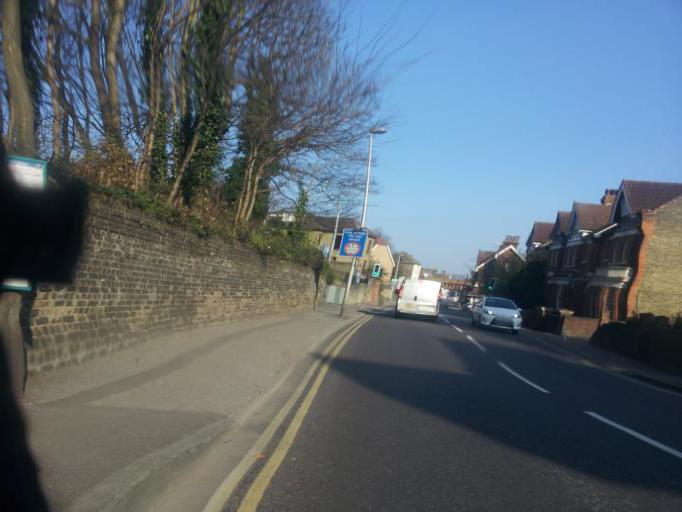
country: GB
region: England
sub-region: Kent
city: Strood
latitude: 51.3964
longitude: 0.4882
